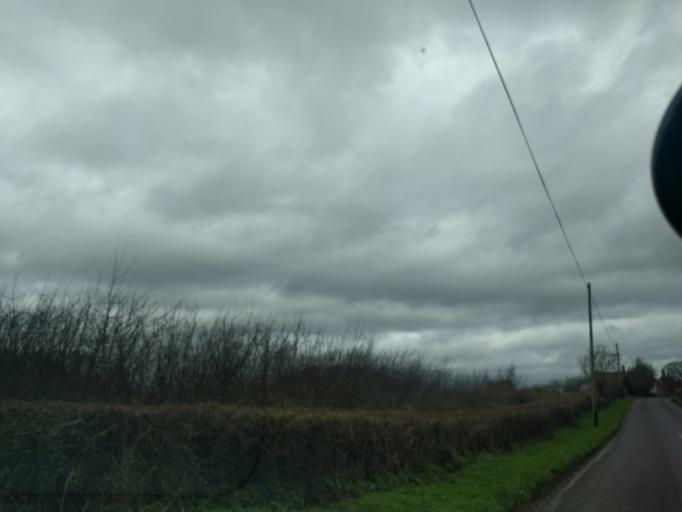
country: GB
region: England
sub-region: Wiltshire
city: Biddestone
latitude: 51.5048
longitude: -2.1992
